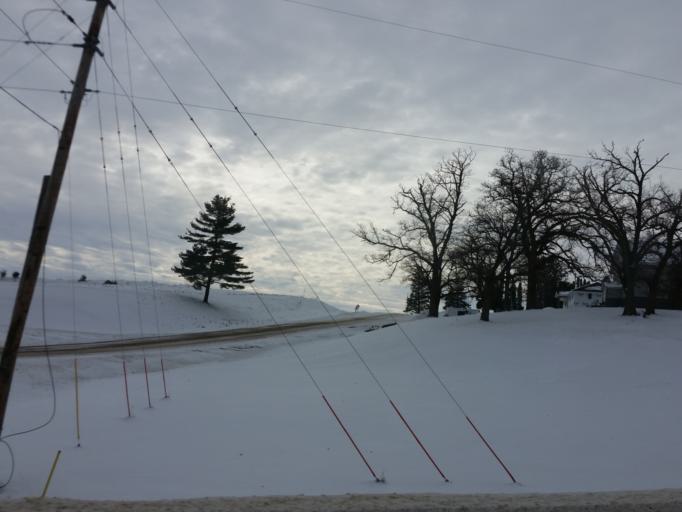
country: US
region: Iowa
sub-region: Dubuque County
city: Peosta
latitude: 42.3821
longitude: -90.7371
